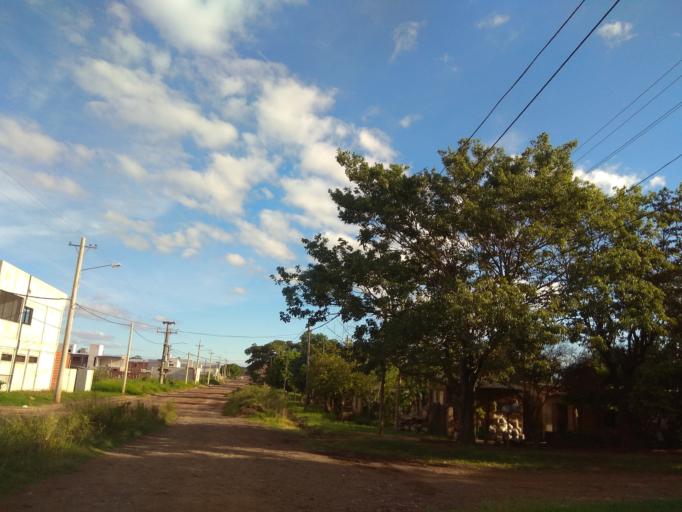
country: AR
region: Misiones
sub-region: Departamento de Capital
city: Posadas
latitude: -27.3821
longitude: -55.9262
